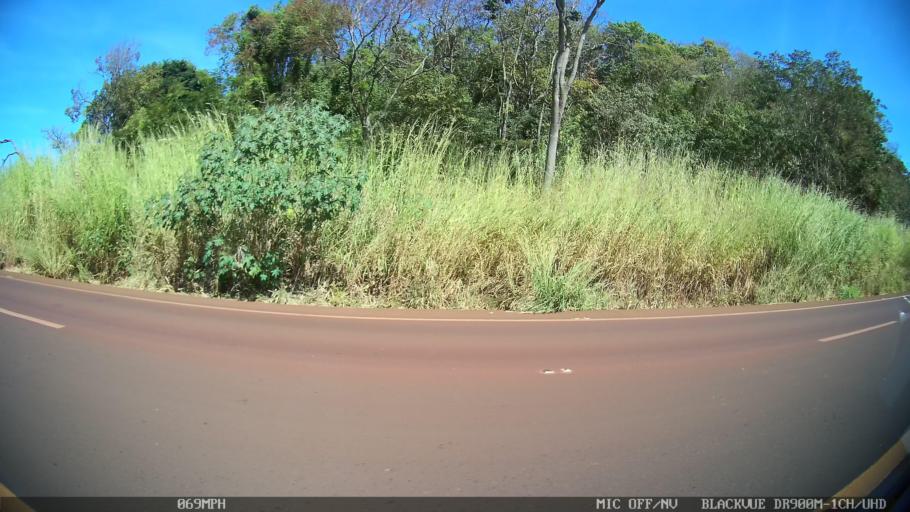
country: BR
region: Sao Paulo
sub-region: Nuporanga
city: Nuporanga
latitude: -20.5504
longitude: -47.6494
